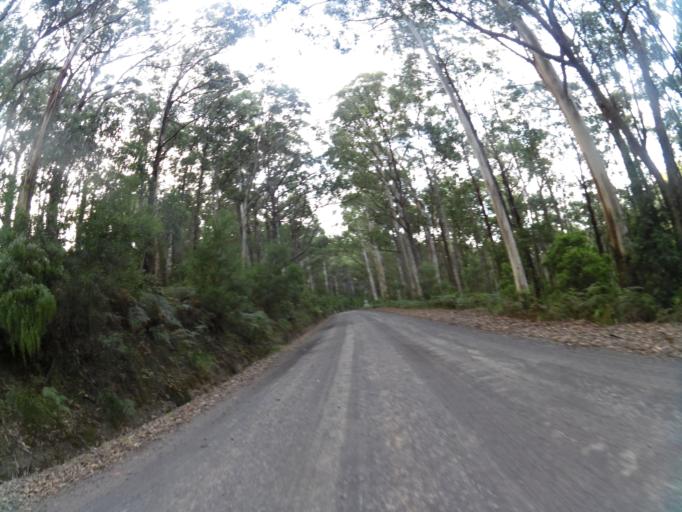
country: AU
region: Victoria
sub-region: Colac-Otway
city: Apollo Bay
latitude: -38.5427
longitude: 143.7308
